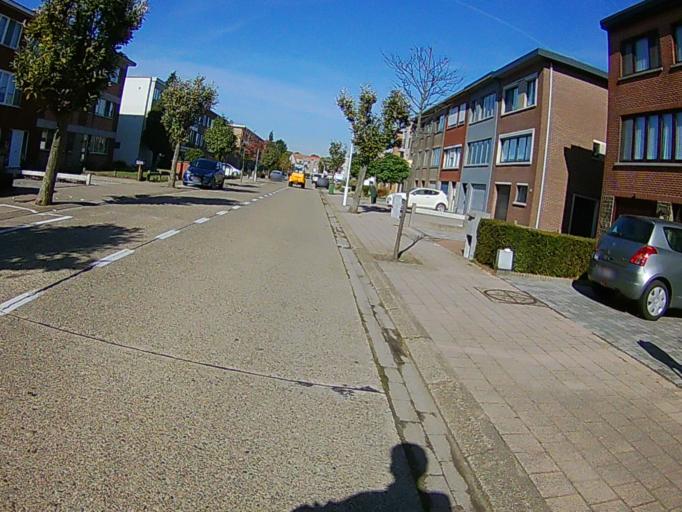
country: BE
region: Flanders
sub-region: Provincie Antwerpen
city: Kapellen
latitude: 51.3062
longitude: 4.4201
